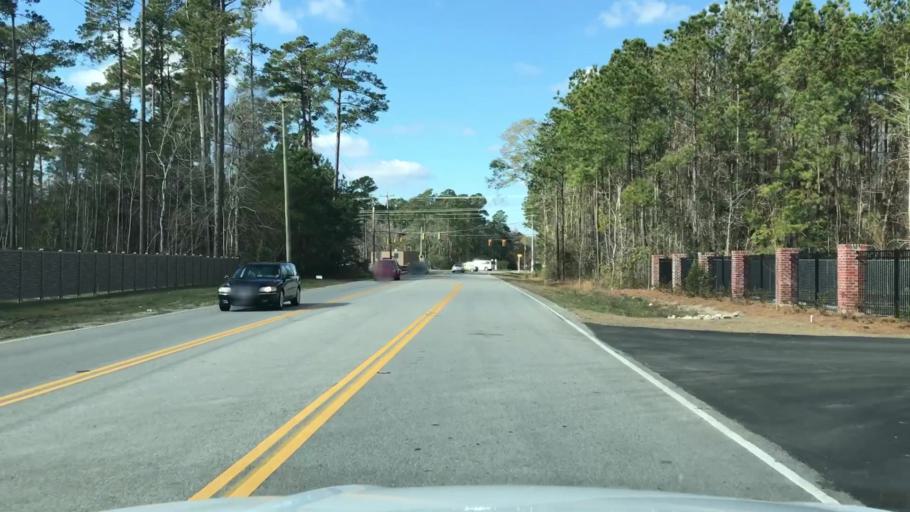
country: US
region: South Carolina
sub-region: Horry County
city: Socastee
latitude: 33.6599
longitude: -79.0109
